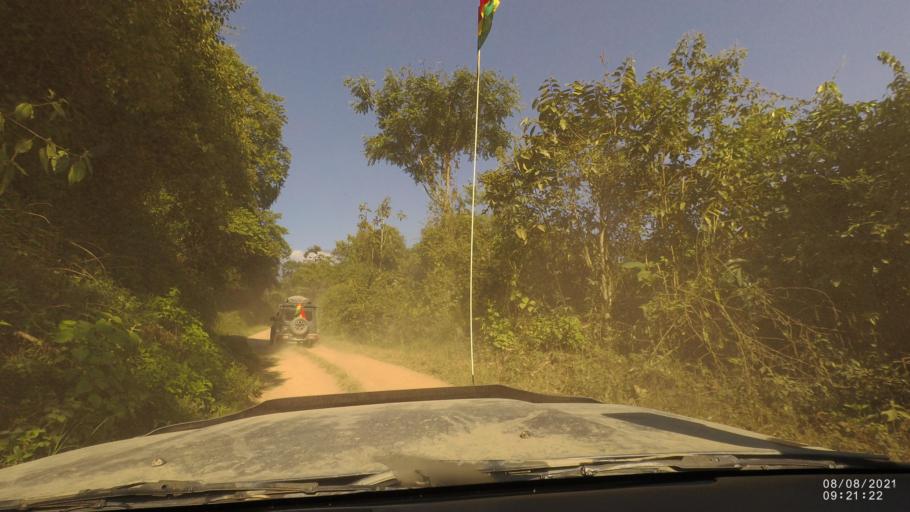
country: BO
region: La Paz
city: Quime
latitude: -16.5723
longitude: -66.7154
